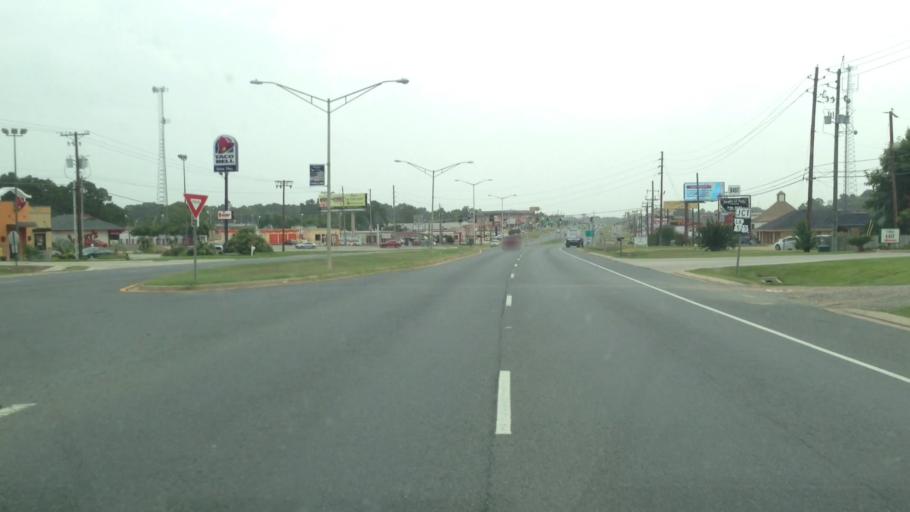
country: US
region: Louisiana
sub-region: De Soto Parish
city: Stonewall
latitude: 32.3943
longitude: -93.8116
